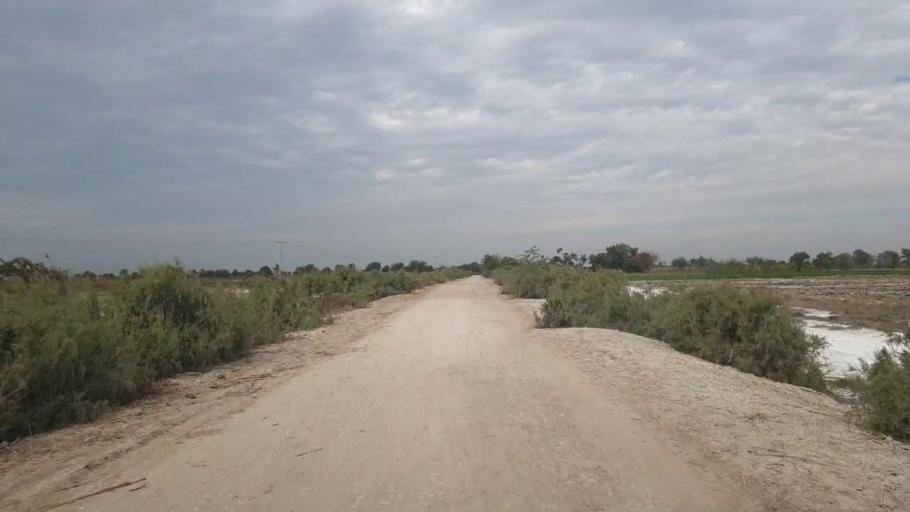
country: PK
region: Sindh
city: Jhol
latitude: 26.0161
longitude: 68.8758
